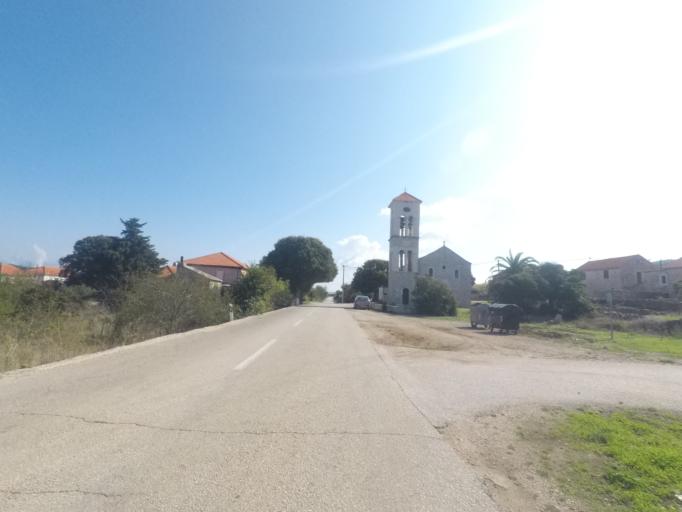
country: HR
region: Splitsko-Dalmatinska
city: Jelsa
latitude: 43.1490
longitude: 16.7929
